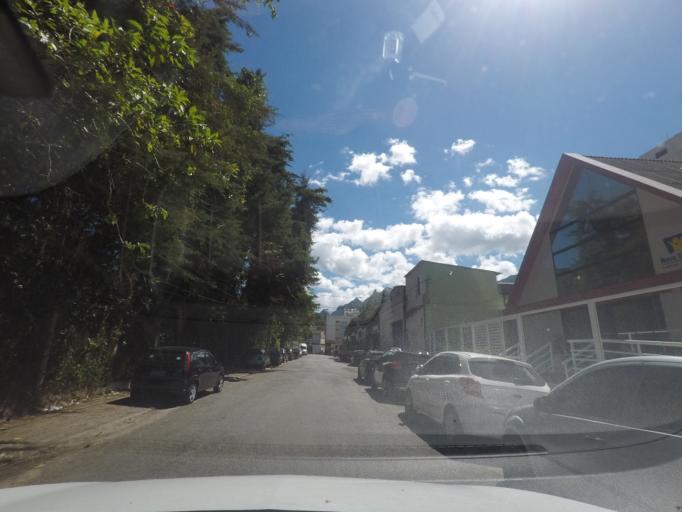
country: BR
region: Rio de Janeiro
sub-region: Teresopolis
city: Teresopolis
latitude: -22.4202
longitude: -42.9735
